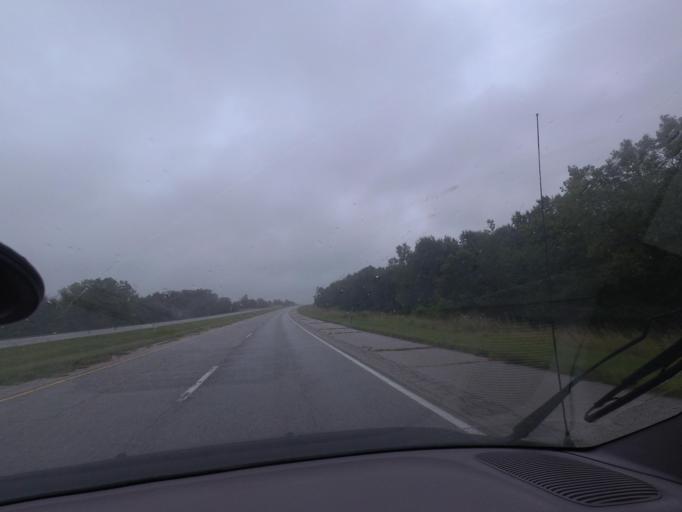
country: US
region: Illinois
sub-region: Pike County
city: Pittsfield
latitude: 39.6853
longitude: -90.8810
